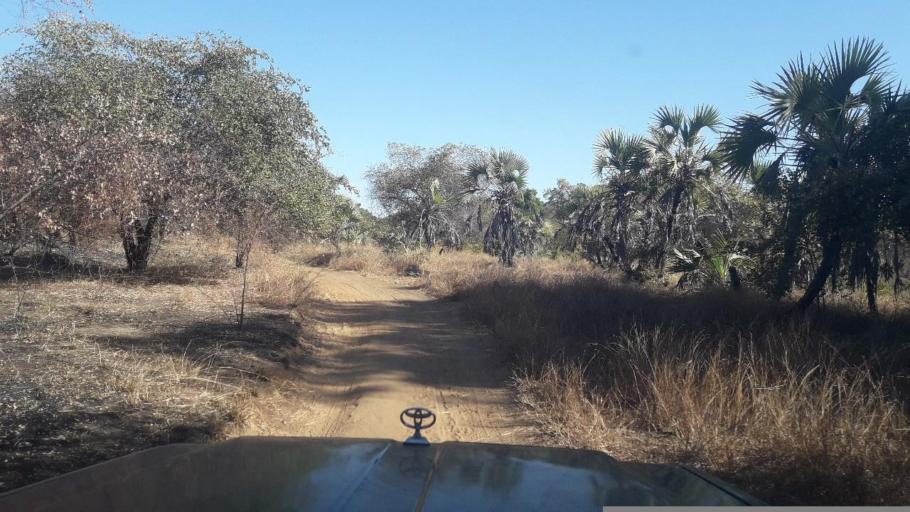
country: MG
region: Boeny
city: Sitampiky
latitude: -16.4018
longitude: 45.5980
